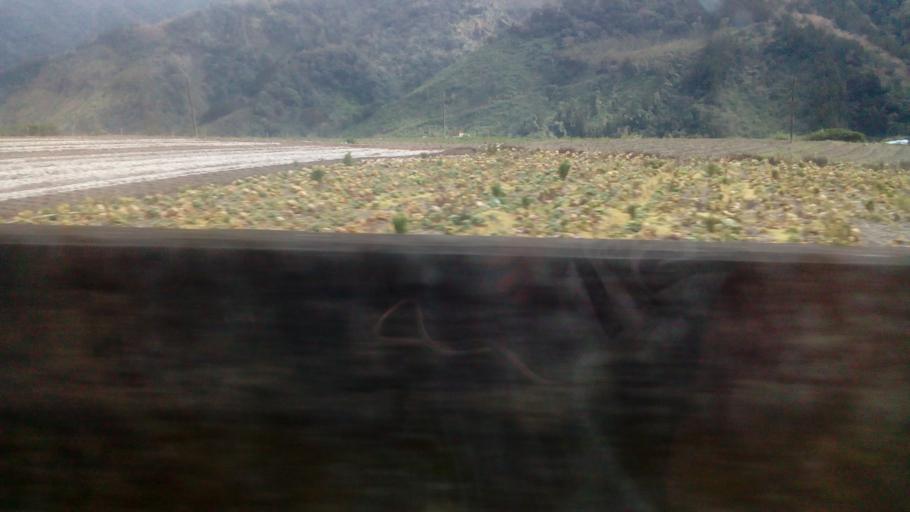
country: TW
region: Taiwan
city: Daxi
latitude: 24.4593
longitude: 121.3942
